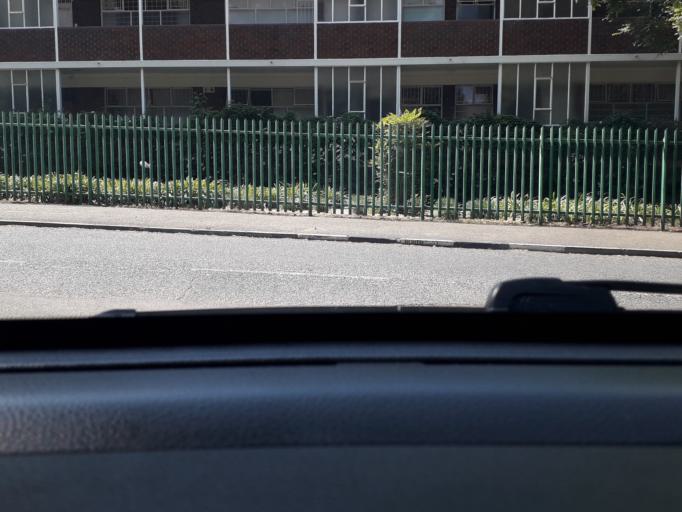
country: ZA
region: Gauteng
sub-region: City of Johannesburg Metropolitan Municipality
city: Johannesburg
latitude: -26.1362
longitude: 28.0509
